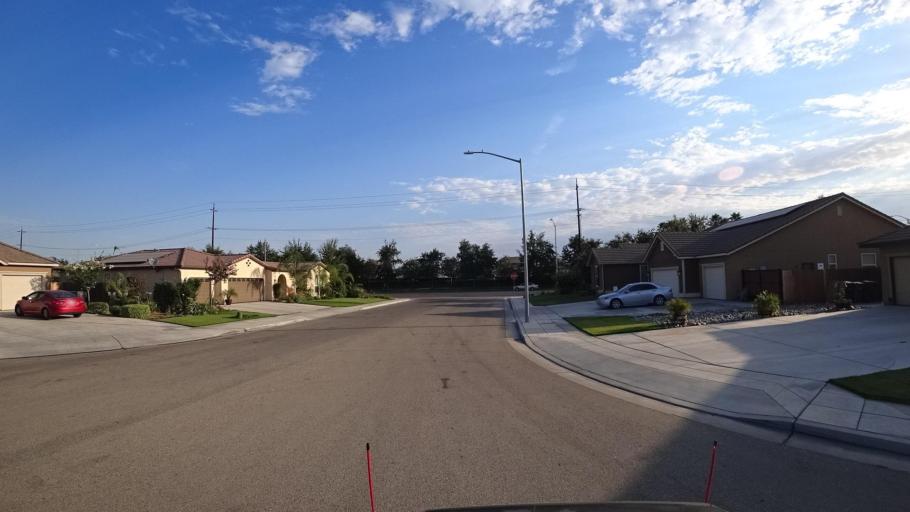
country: US
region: California
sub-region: Fresno County
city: Sunnyside
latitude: 36.7142
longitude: -119.7041
